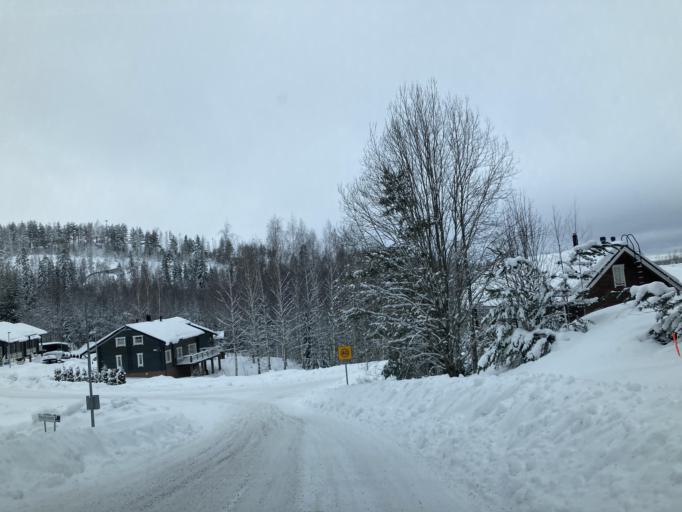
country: FI
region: Central Finland
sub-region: Jaemsae
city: Jaemsae
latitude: 61.8755
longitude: 25.3131
